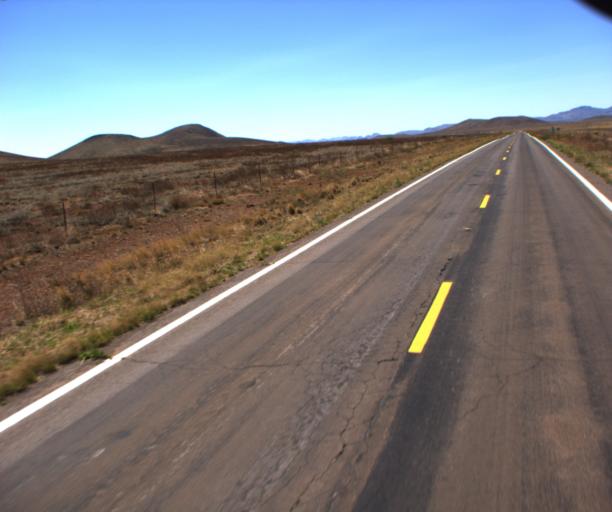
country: US
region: Arizona
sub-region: Cochise County
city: Douglas
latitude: 31.5907
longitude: -109.2430
